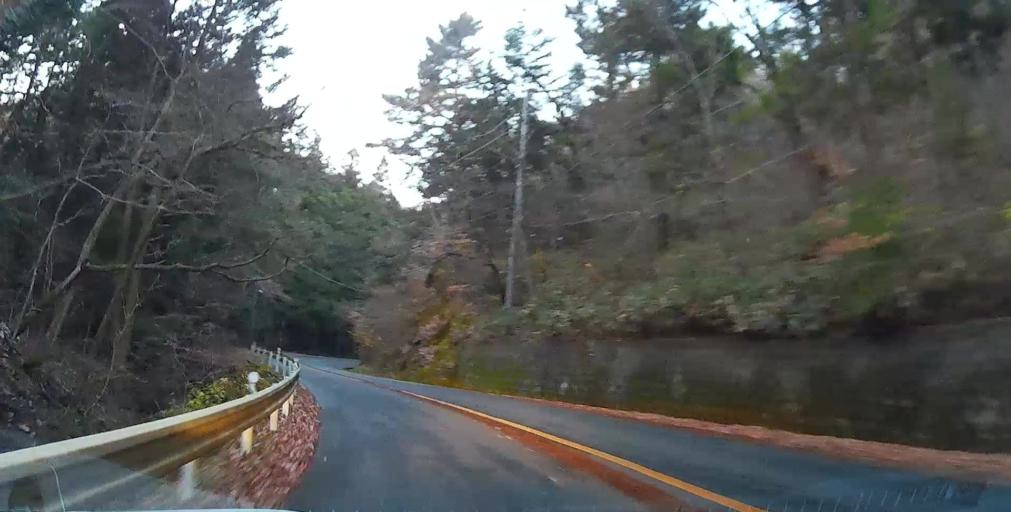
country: JP
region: Yamanashi
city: Uenohara
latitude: 35.5813
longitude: 139.1780
